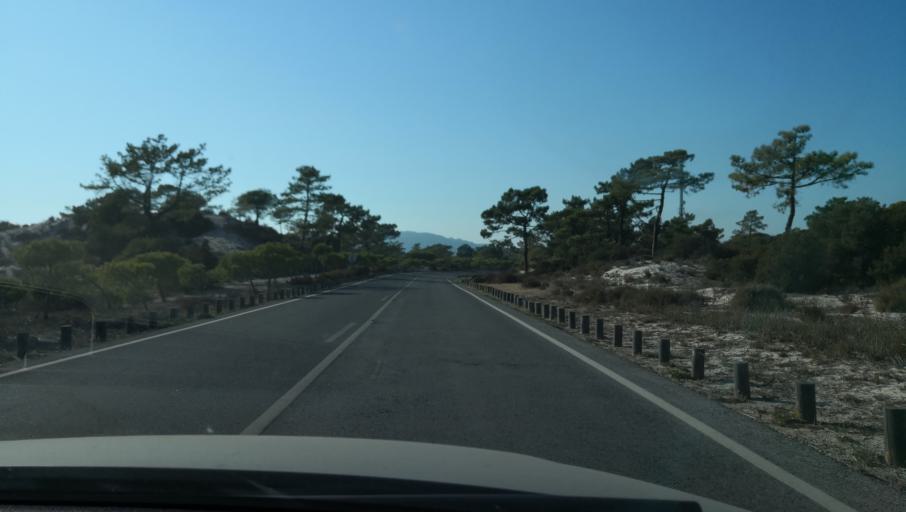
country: PT
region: Setubal
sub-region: Setubal
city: Setubal
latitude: 38.4687
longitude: -8.8814
